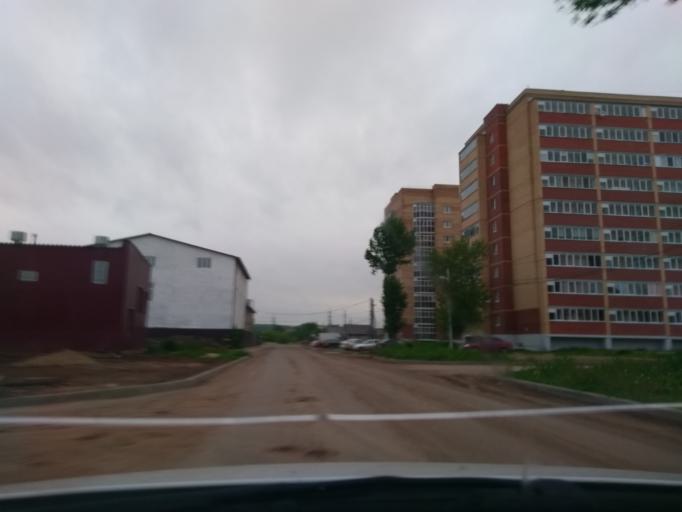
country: RU
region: Perm
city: Froly
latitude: 57.9214
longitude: 56.2691
